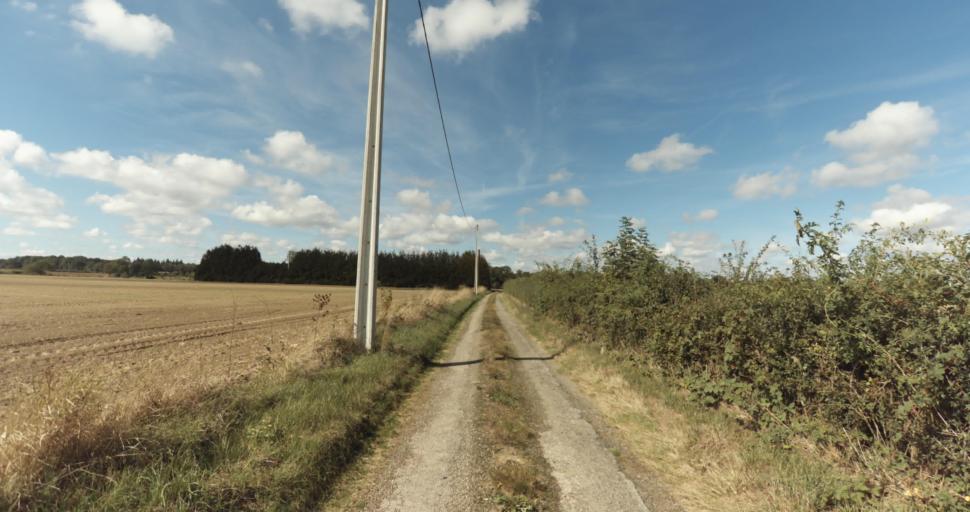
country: FR
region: Lower Normandy
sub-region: Departement du Calvados
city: Orbec
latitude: 48.9588
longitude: 0.4026
